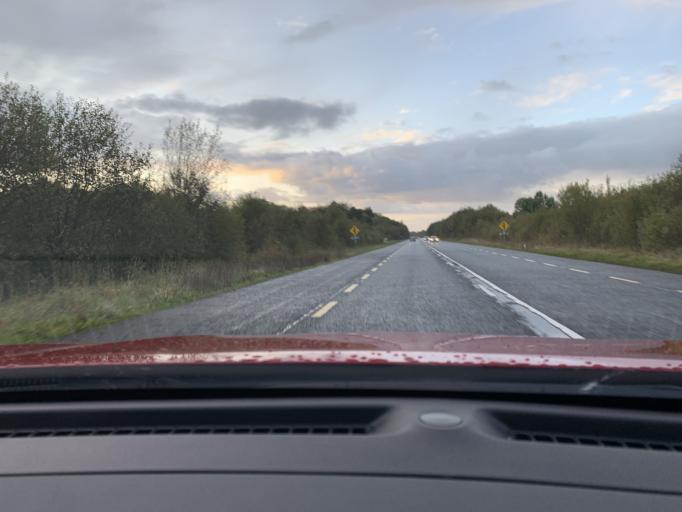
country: IE
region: Connaught
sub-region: County Leitrim
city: Carrick-on-Shannon
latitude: 53.9508
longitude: -8.1501
